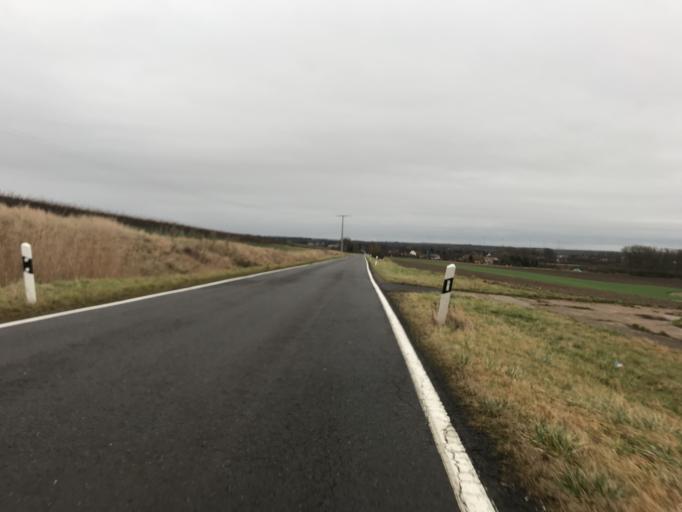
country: DE
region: Rheinland-Pfalz
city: Sorgenloch
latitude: 49.8691
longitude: 8.2136
